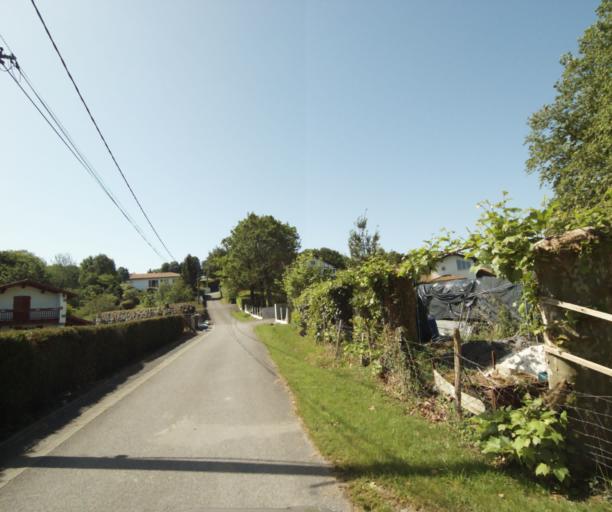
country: FR
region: Aquitaine
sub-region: Departement des Pyrenees-Atlantiques
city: Villefranque
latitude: 43.4603
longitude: -1.4446
